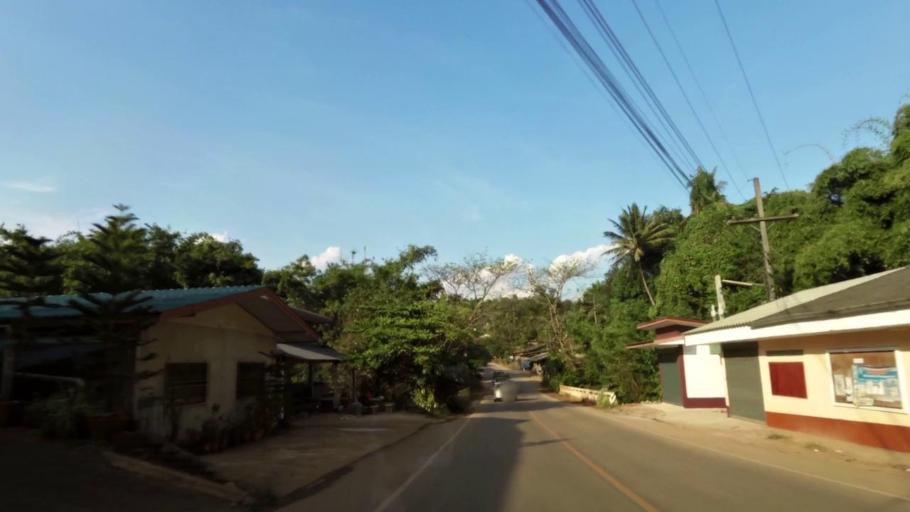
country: TH
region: Chiang Rai
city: Khun Tan
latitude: 19.8657
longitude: 100.3990
